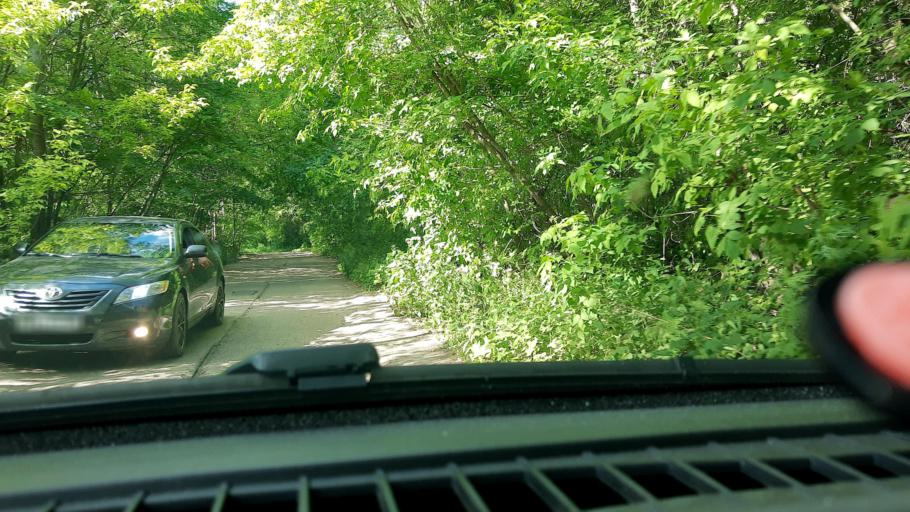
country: RU
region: Nizjnij Novgorod
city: Nizhniy Novgorod
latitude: 56.2564
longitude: 43.9650
